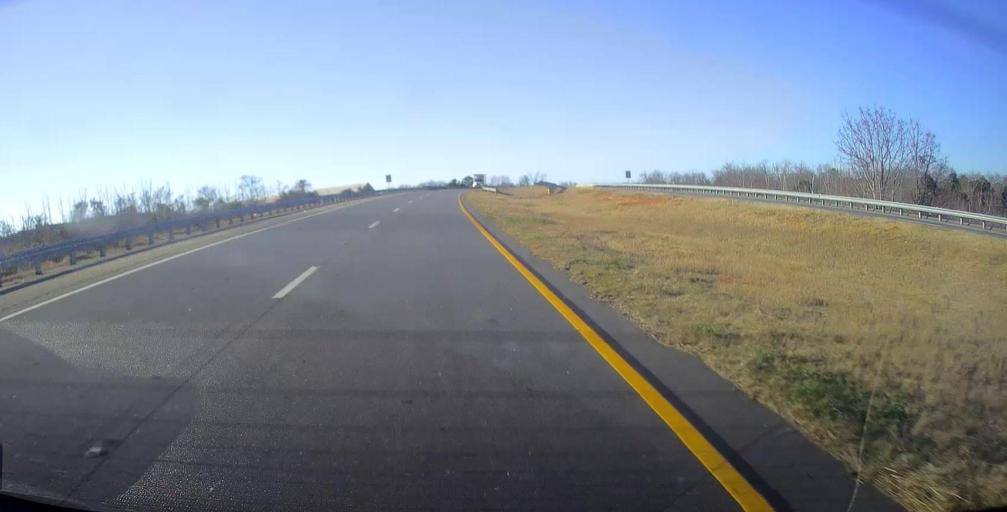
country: US
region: Georgia
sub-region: Sumter County
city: Americus
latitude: 31.8945
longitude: -84.2593
